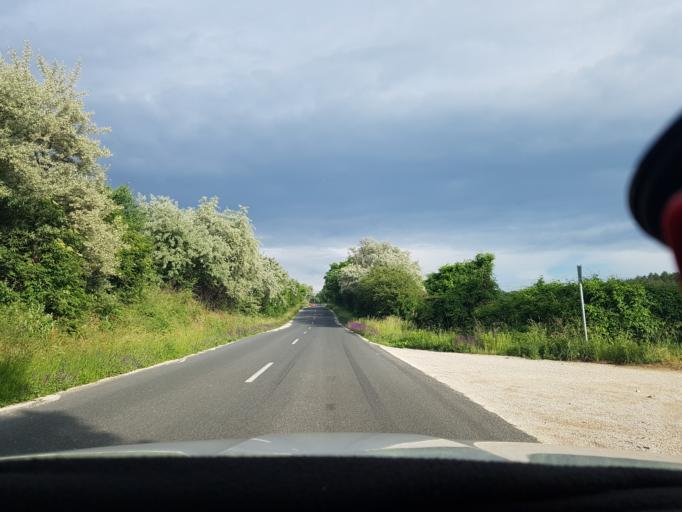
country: HU
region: Komarom-Esztergom
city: Labatlan
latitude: 47.7302
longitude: 18.5304
